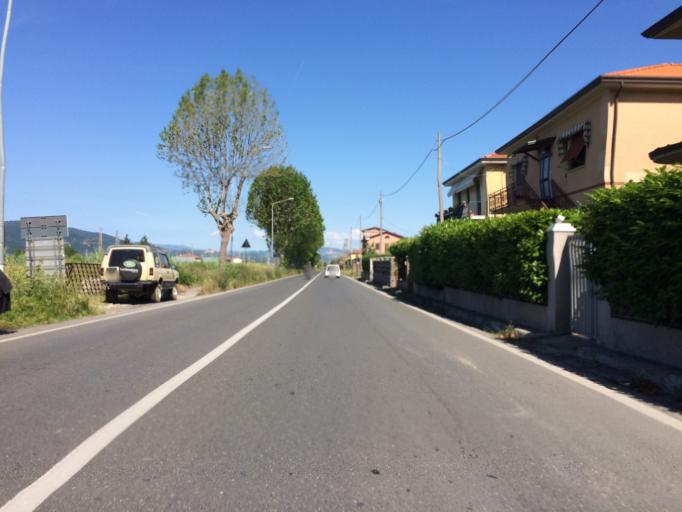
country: IT
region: Liguria
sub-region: Provincia di La Spezia
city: Casano-Dogana-Isola
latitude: 44.0731
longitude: 10.0199
